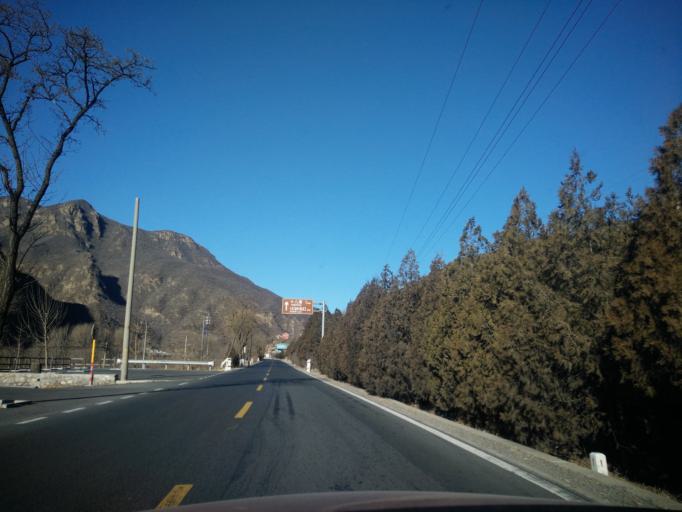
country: CN
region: Beijing
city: Wangping
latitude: 40.0097
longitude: 115.9280
